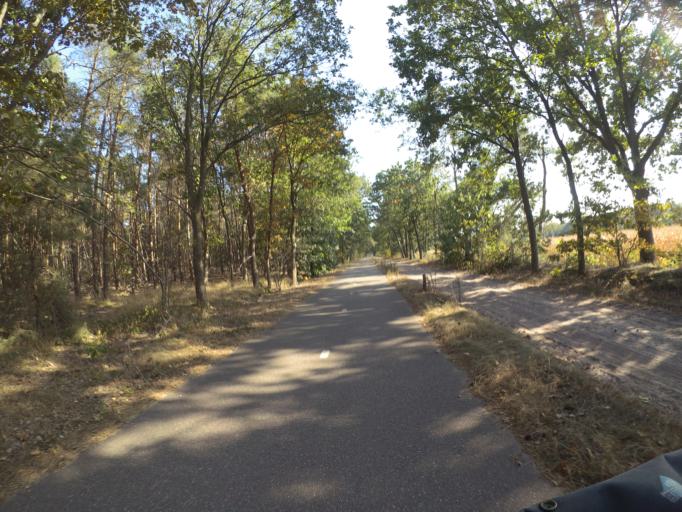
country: NL
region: North Brabant
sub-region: Gemeente Oirschot
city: Oostelbeers
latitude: 51.4767
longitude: 5.2827
